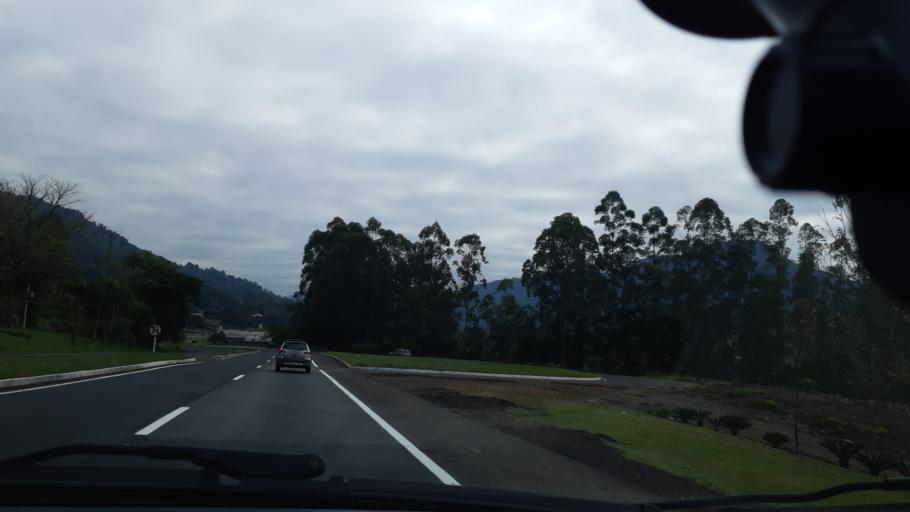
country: BR
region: Rio Grande do Sul
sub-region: Farroupilha
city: Farroupilha
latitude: -29.4028
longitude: -51.3548
